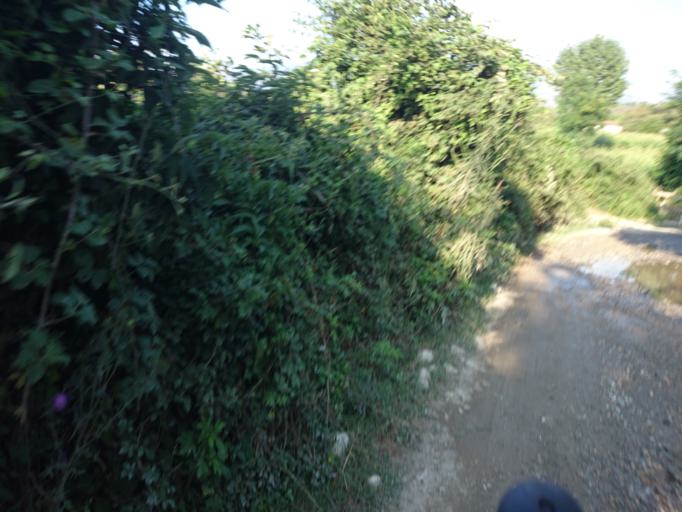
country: AL
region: Diber
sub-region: Rrethi i Dibres
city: Arras
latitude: 41.7350
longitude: 20.3414
